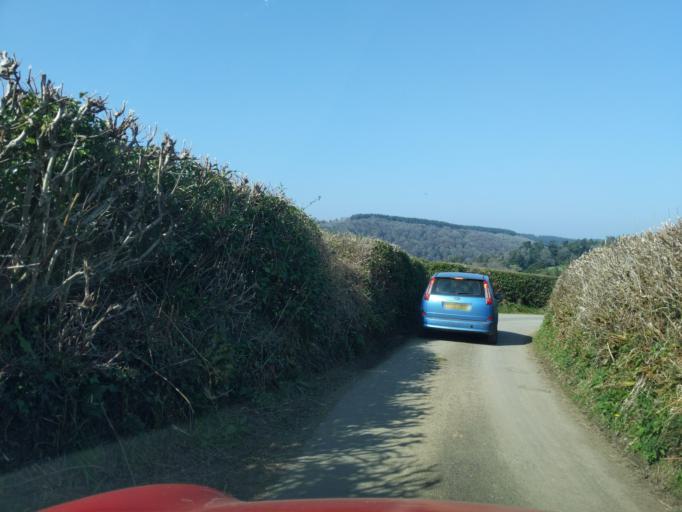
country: GB
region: England
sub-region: Devon
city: Bere Alston
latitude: 50.4520
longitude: -4.1520
